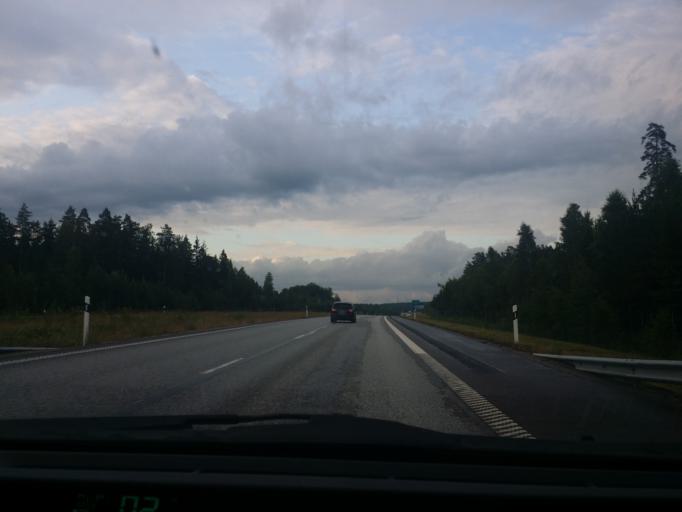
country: SE
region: Vaestmanland
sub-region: Kopings Kommun
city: Koping
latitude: 59.4918
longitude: 15.9201
